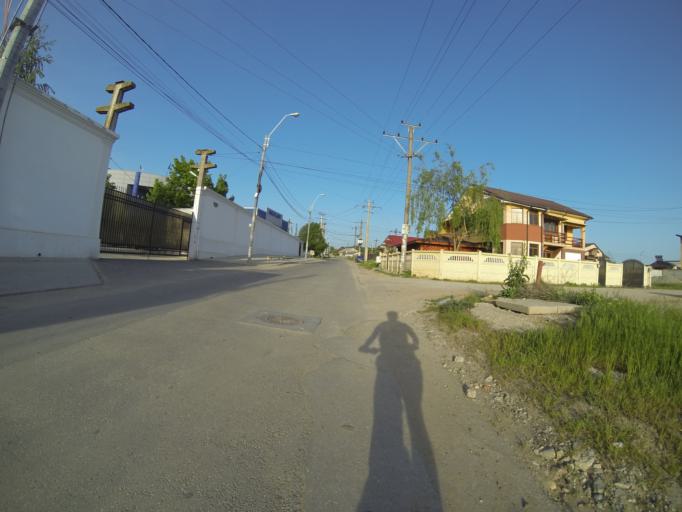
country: RO
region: Dolj
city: Craiova
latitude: 44.3223
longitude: 23.8455
